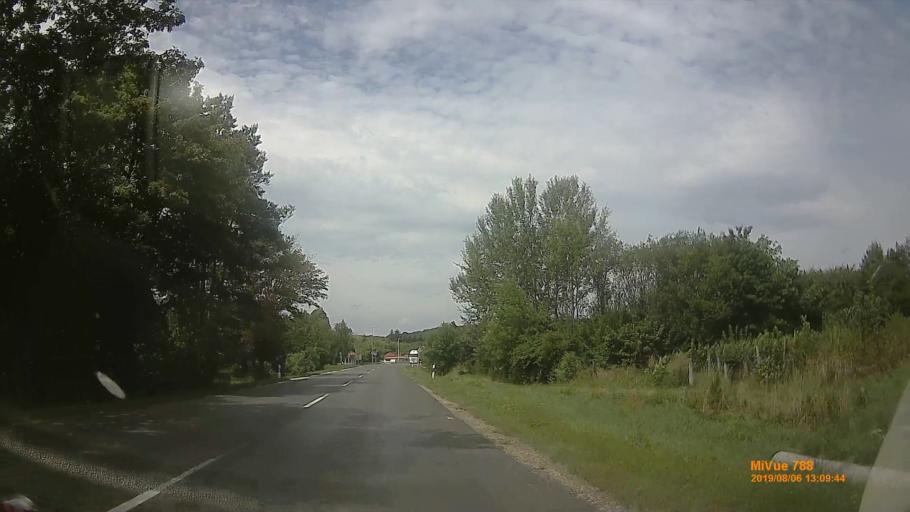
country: HU
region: Vas
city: Koszeg
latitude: 47.4005
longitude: 16.5404
